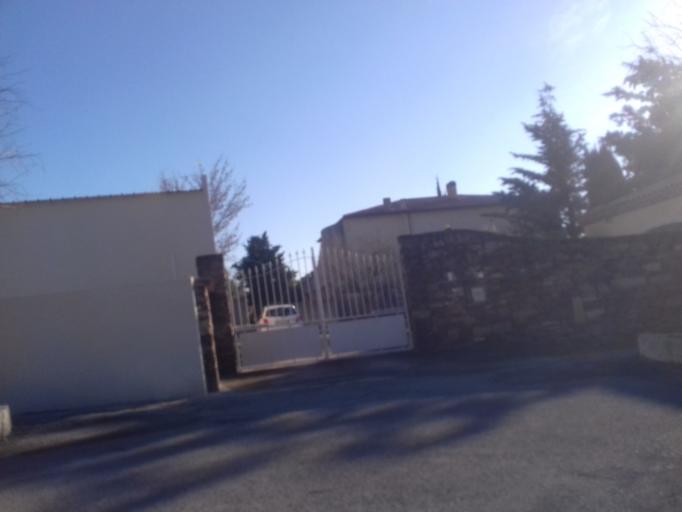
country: FR
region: Provence-Alpes-Cote d'Azur
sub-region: Departement des Bouches-du-Rhone
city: Marignane
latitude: 43.4052
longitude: 5.2220
